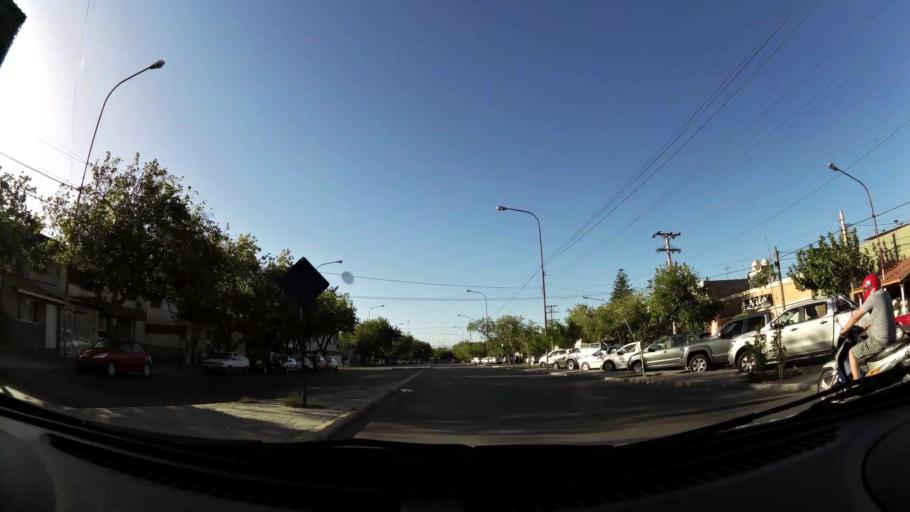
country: AR
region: San Juan
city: San Juan
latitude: -31.5440
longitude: -68.5208
